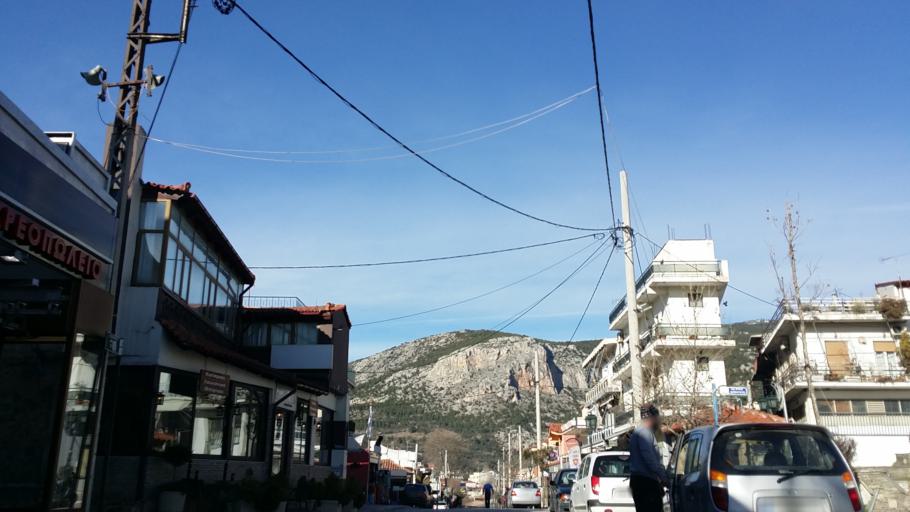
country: GR
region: Attica
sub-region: Nomarchia Dytikis Attikis
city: Fyli
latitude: 38.1026
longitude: 23.6690
